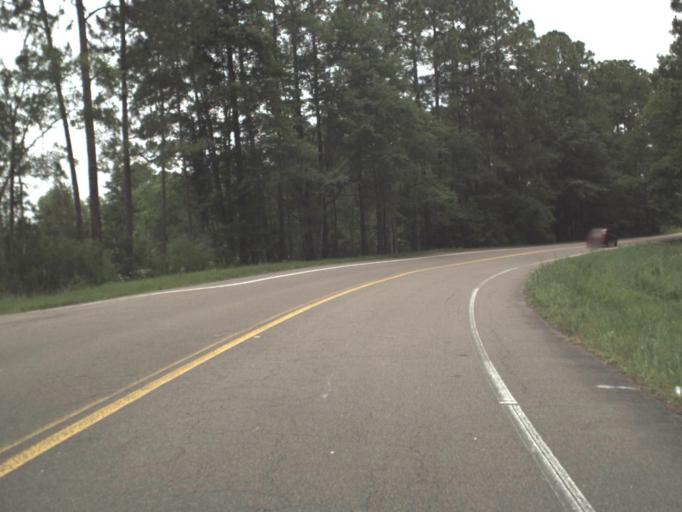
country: US
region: Florida
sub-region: Duval County
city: Jacksonville
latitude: 30.4668
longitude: -81.6774
